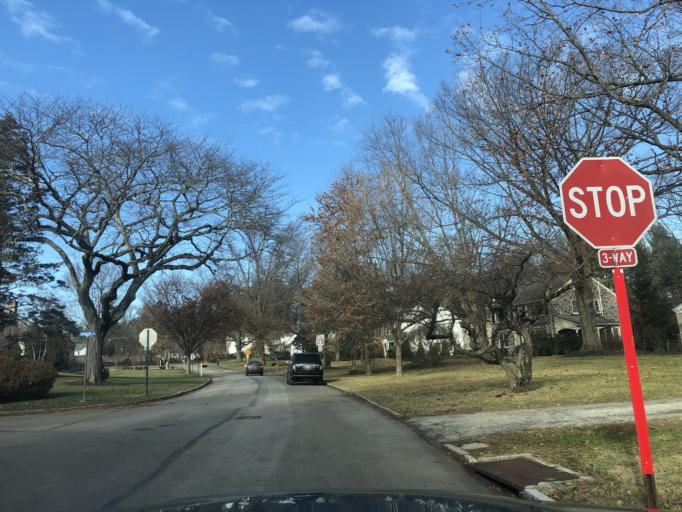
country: US
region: Pennsylvania
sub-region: Delaware County
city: Radnor
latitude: 40.0293
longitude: -75.3434
